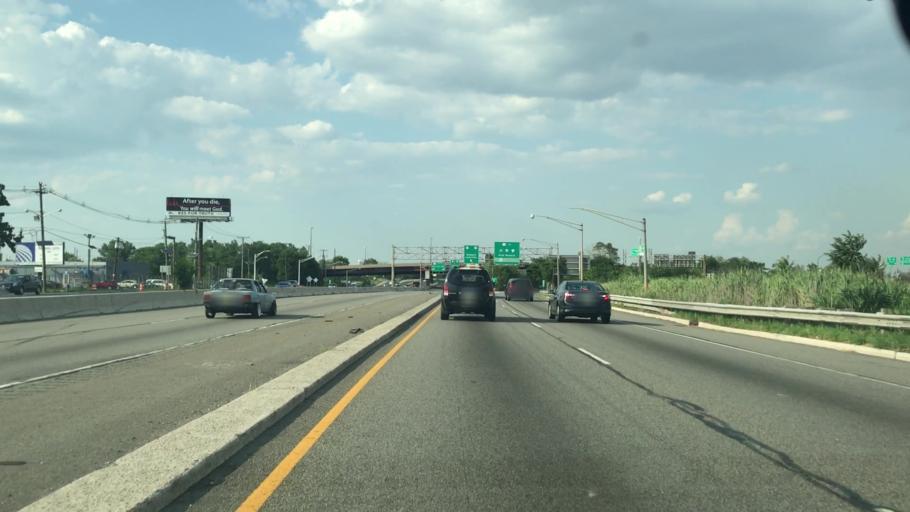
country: US
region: New Jersey
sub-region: Essex County
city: Newark
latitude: 40.7033
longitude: -74.1841
